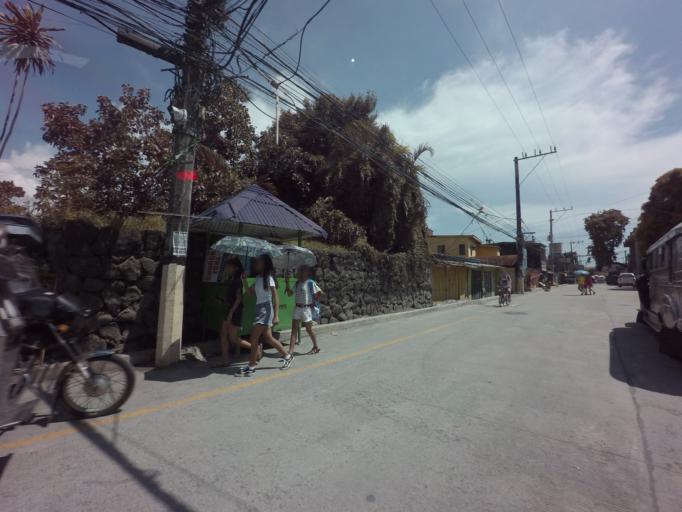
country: PH
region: Calabarzon
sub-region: Province of Rizal
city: Las Pinas
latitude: 14.4648
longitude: 120.9708
